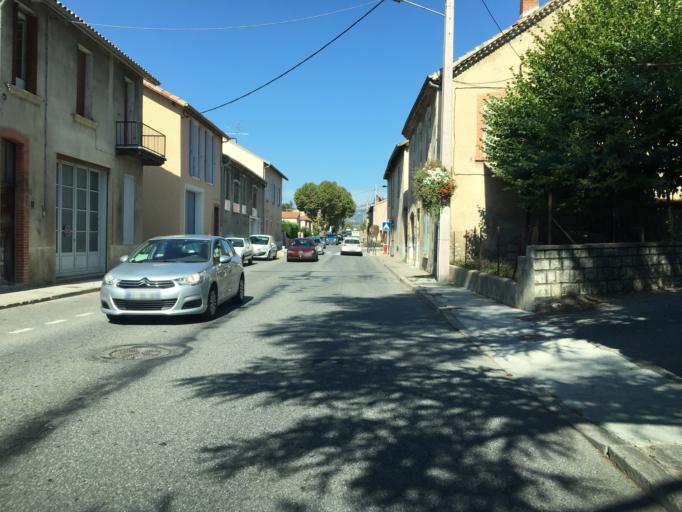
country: FR
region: Provence-Alpes-Cote d'Azur
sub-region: Departement des Hautes-Alpes
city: Laragne-Monteglin
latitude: 44.3150
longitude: 5.8195
